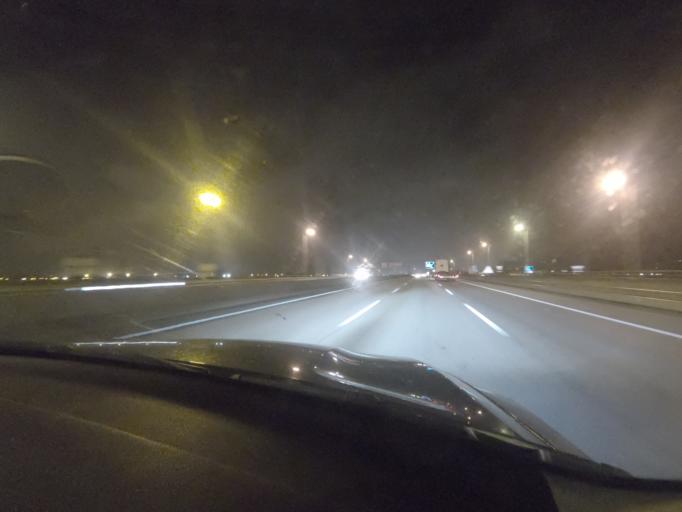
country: PT
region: Lisbon
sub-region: Alenquer
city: Carregado
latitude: 39.0138
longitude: -8.9663
